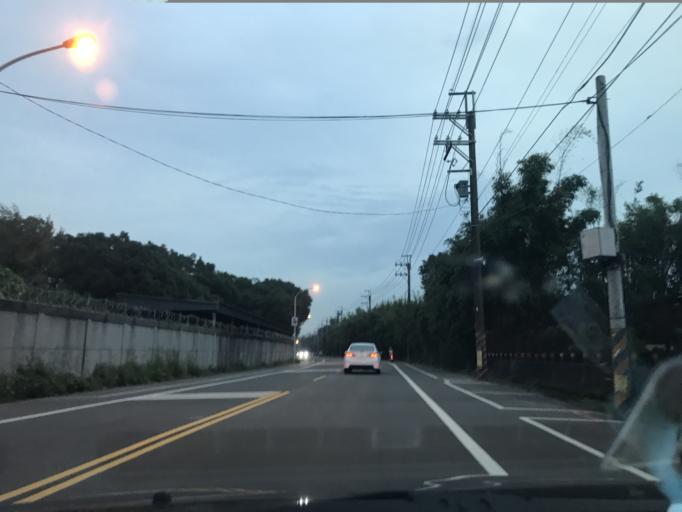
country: TW
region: Taiwan
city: Daxi
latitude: 24.9237
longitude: 121.2375
